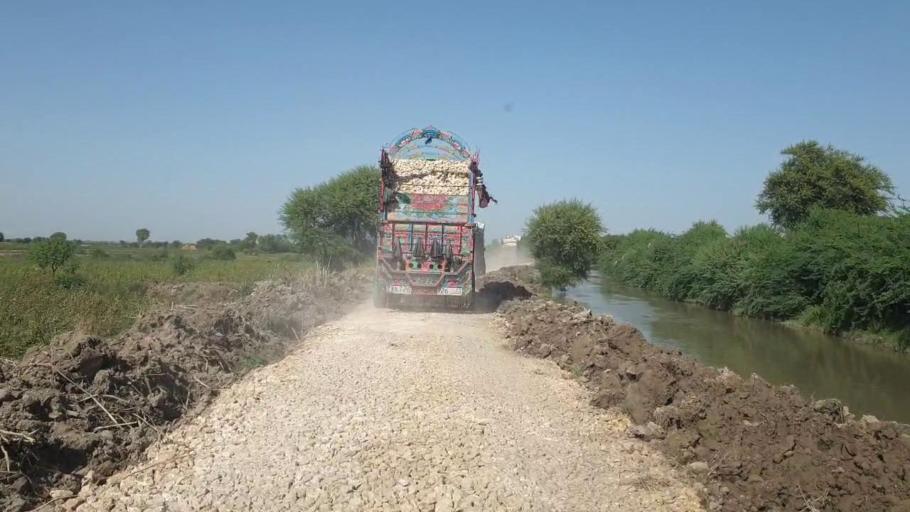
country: PK
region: Sindh
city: Kadhan
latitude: 24.5297
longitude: 69.0006
